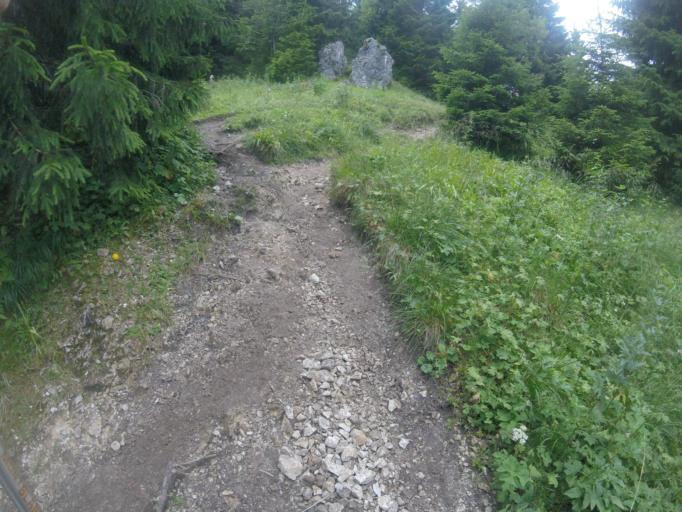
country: SK
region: Zilinsky
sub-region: Okres Zilina
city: Terchova
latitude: 49.2425
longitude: 19.1071
